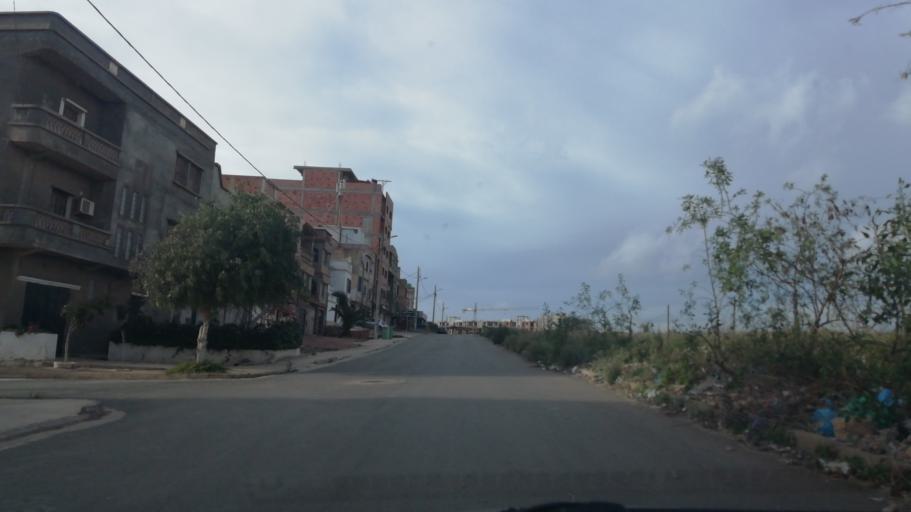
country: DZ
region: Oran
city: Bir el Djir
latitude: 35.7302
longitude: -0.5681
